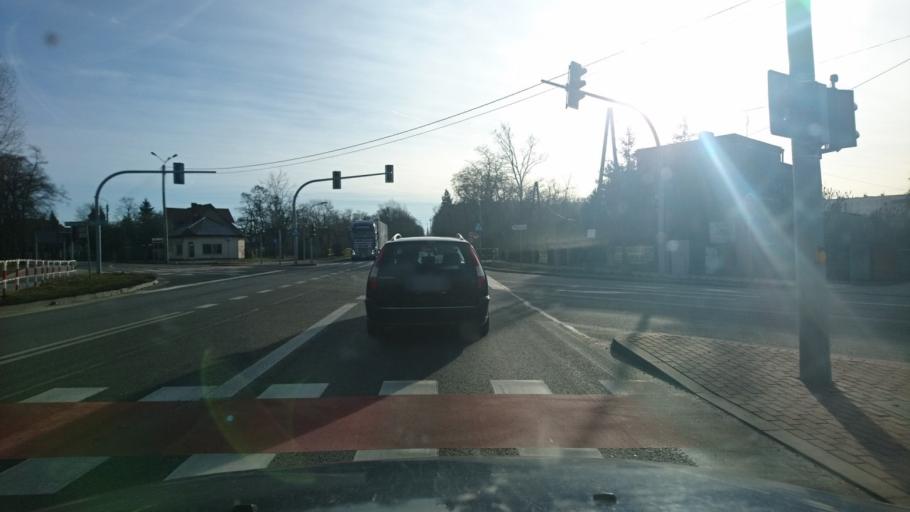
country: PL
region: Greater Poland Voivodeship
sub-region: Powiat ostrzeszowski
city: Ostrzeszow
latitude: 51.4287
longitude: 17.9203
